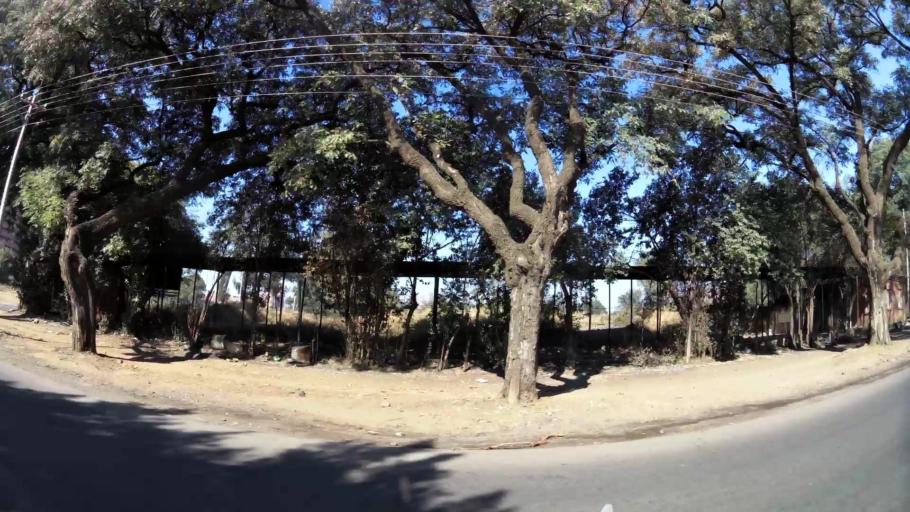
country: ZA
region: Gauteng
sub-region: City of Tshwane Metropolitan Municipality
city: Pretoria
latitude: -25.7443
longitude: 28.1767
